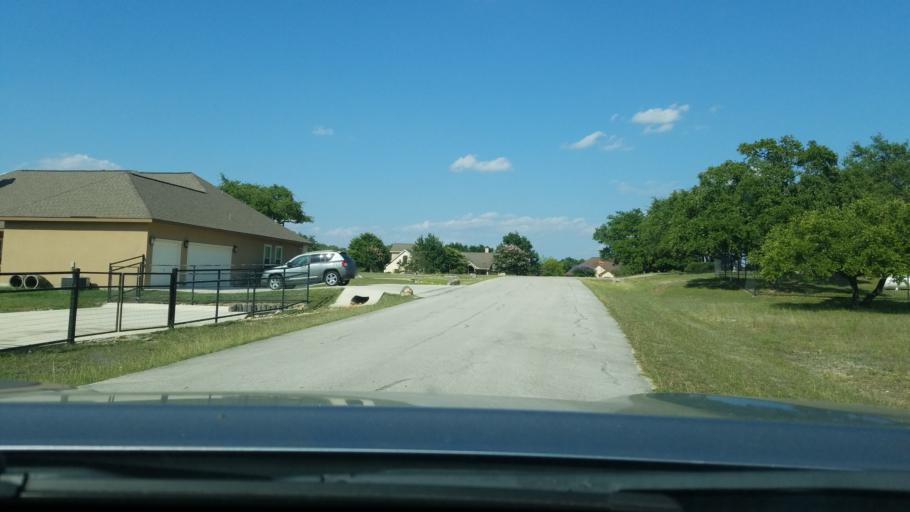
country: US
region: Texas
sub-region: Comal County
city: Bulverde
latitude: 29.8304
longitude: -98.4047
